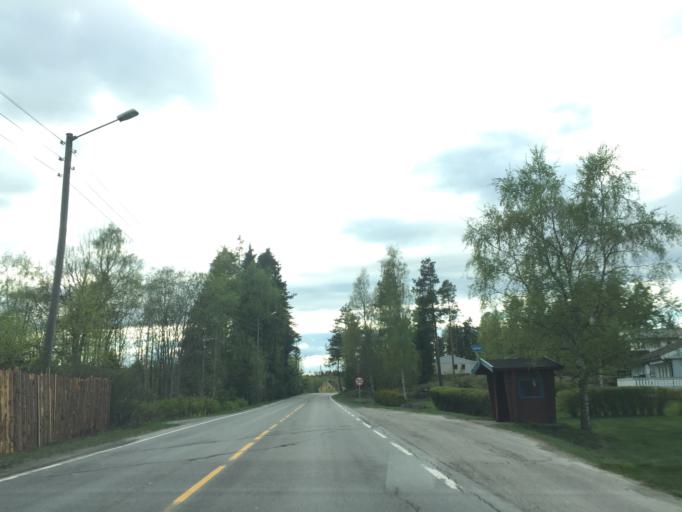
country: NO
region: Hedmark
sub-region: Eidskog
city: Skotterud
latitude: 59.9772
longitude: 12.1399
